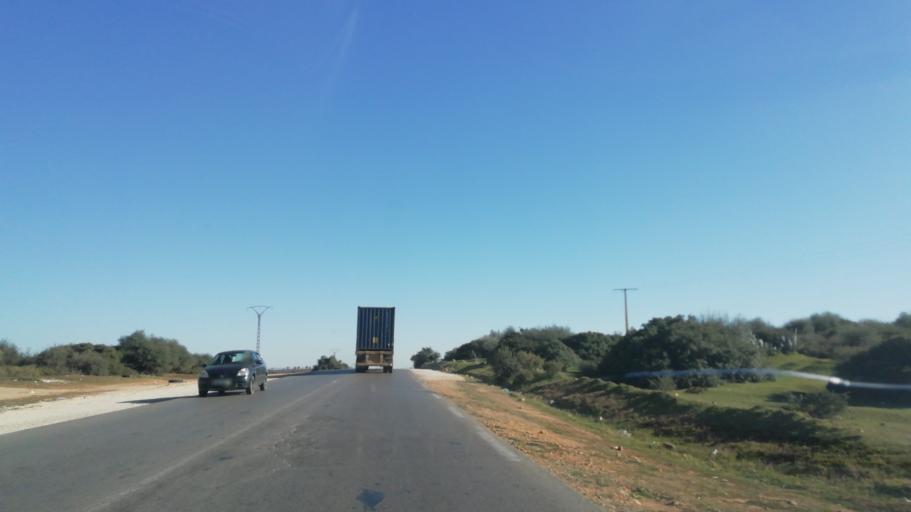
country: DZ
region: Relizane
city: Smala
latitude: 35.6914
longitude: 0.7899
